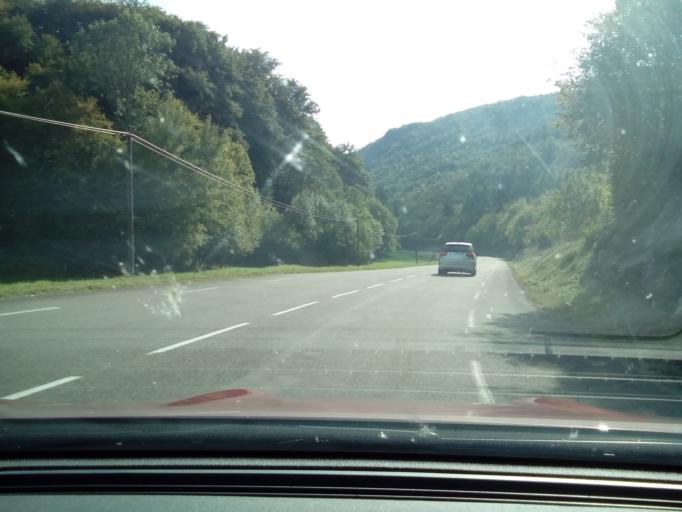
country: FR
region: Rhone-Alpes
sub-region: Departement de la Drome
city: Saint-Laurent-en-Royans
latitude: 44.9844
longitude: 5.4015
